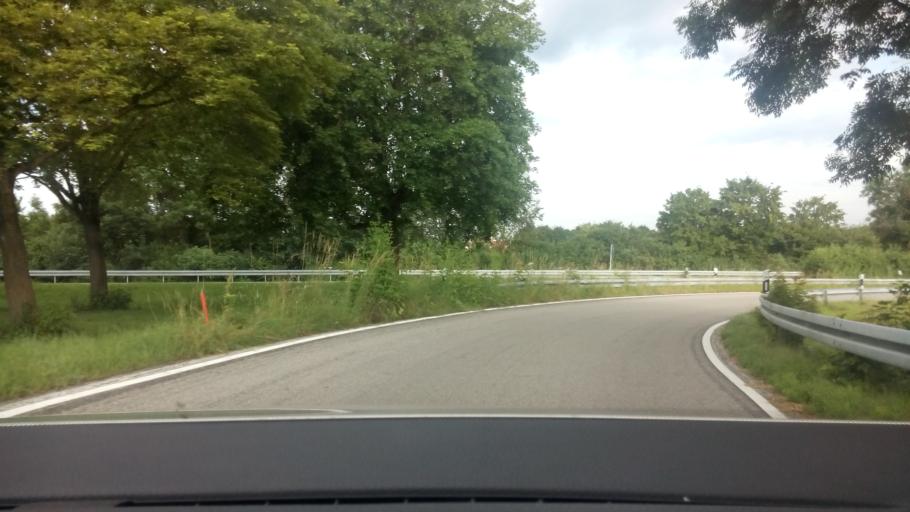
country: DE
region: Bavaria
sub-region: Upper Bavaria
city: Dachau
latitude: 48.2397
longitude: 11.4510
